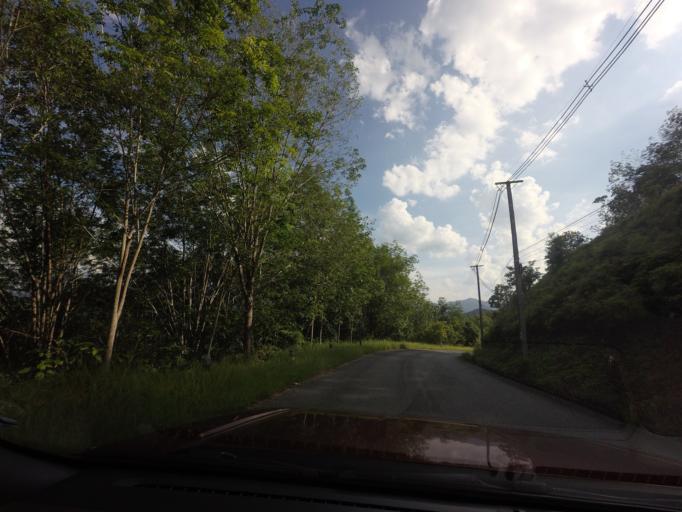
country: TH
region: Yala
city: Than To
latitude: 6.1371
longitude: 101.2937
